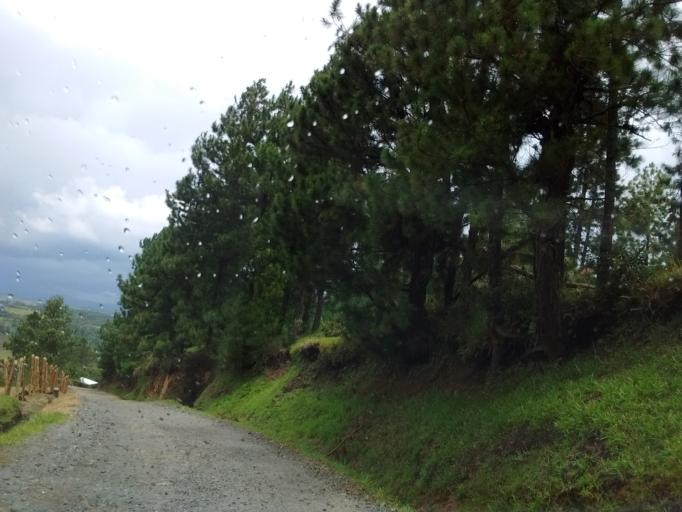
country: CO
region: Cauca
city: Cajibio
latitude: 2.5642
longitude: -76.6353
